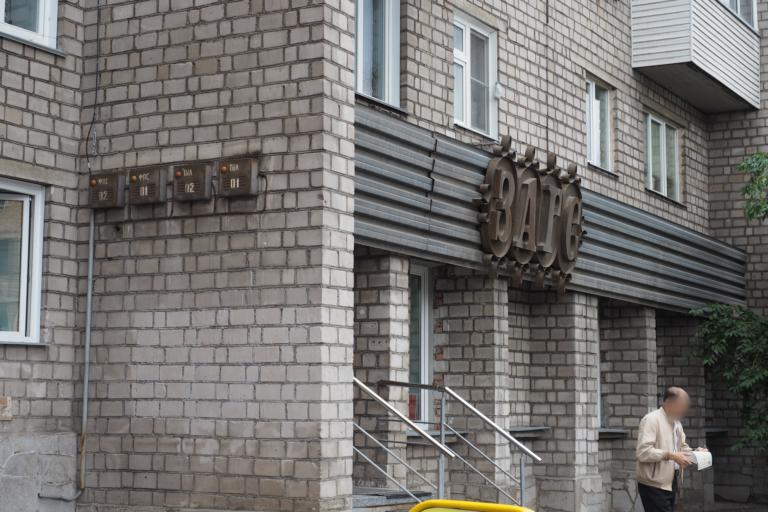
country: RU
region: Krasnoyarskiy
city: Krasnoyarsk
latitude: 56.0130
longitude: 92.8623
